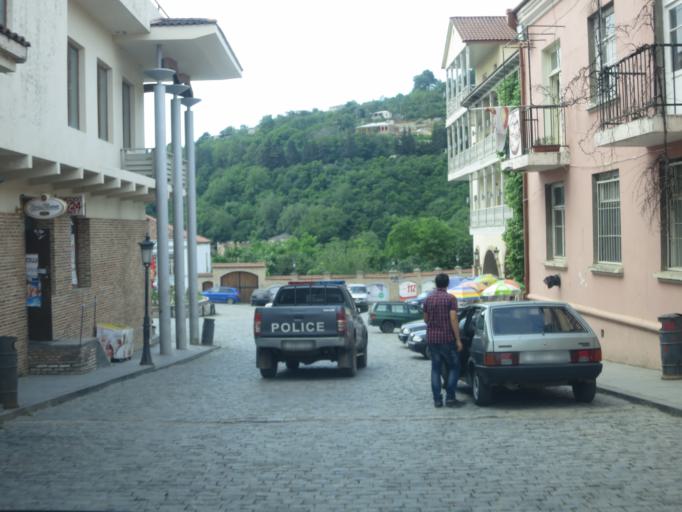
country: GE
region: Kakheti
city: Sighnaghi
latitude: 41.6180
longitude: 45.9217
